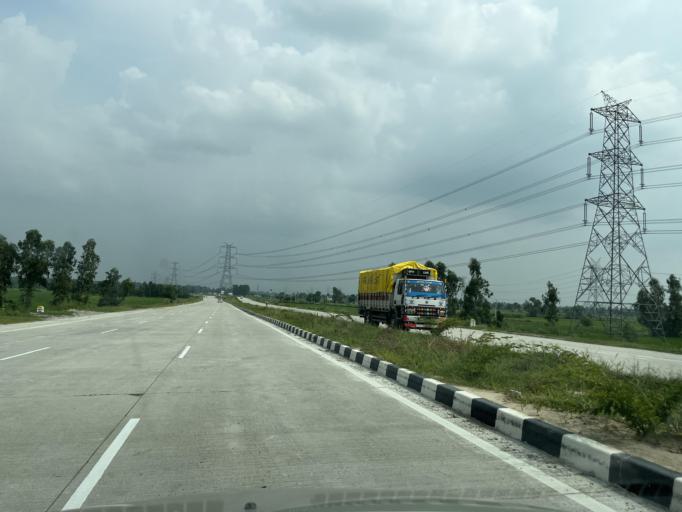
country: IN
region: Uttarakhand
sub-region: Udham Singh Nagar
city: Jaspur
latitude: 29.2870
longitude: 78.8553
